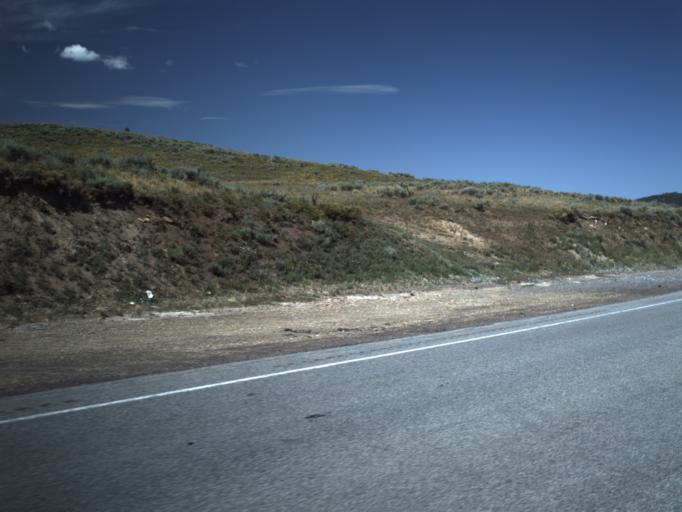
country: US
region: Utah
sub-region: Carbon County
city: Helper
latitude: 39.9249
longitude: -111.0699
